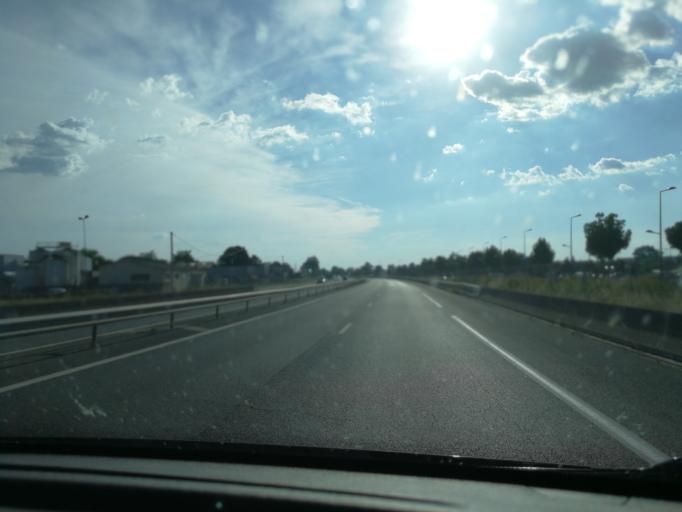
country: FR
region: Midi-Pyrenees
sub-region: Departement du Tarn
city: Le Sequestre
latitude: 43.9183
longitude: 2.1104
